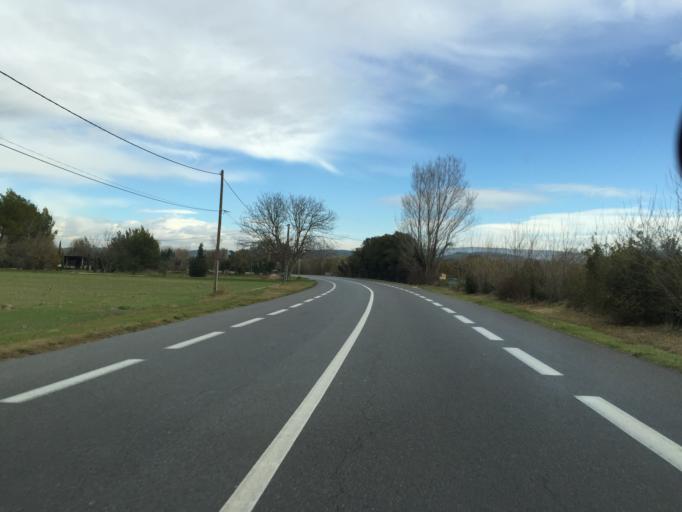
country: FR
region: Provence-Alpes-Cote d'Azur
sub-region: Departement du Vaucluse
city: Velleron
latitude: 43.9800
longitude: 5.0115
